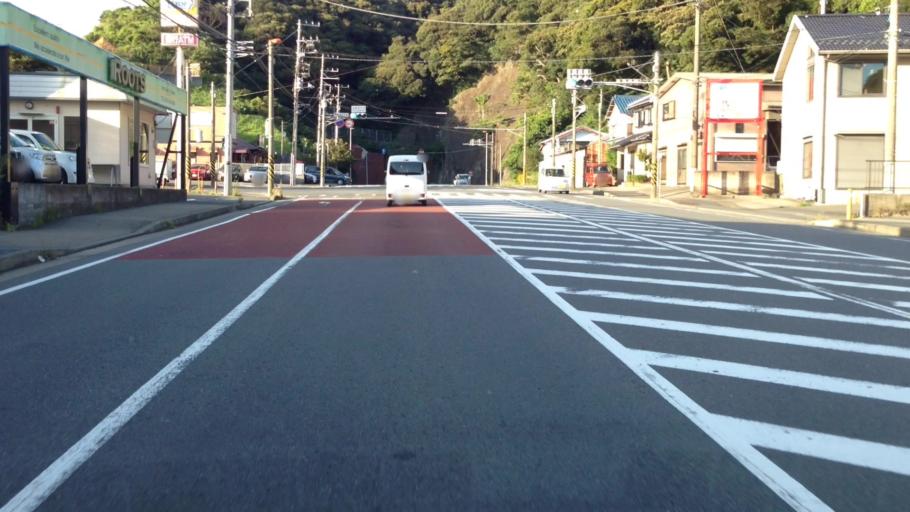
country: JP
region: Kanagawa
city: Yokosuka
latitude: 35.2322
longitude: 139.6572
